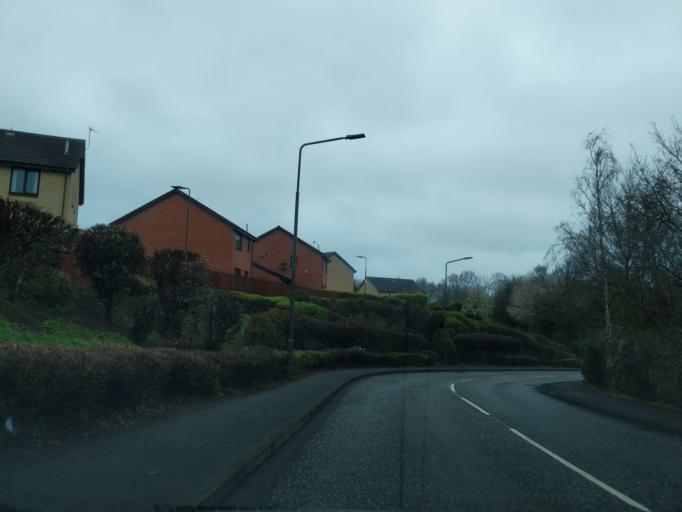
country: GB
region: Scotland
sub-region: East Lothian
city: Musselburgh
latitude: 55.9387
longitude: -3.0730
